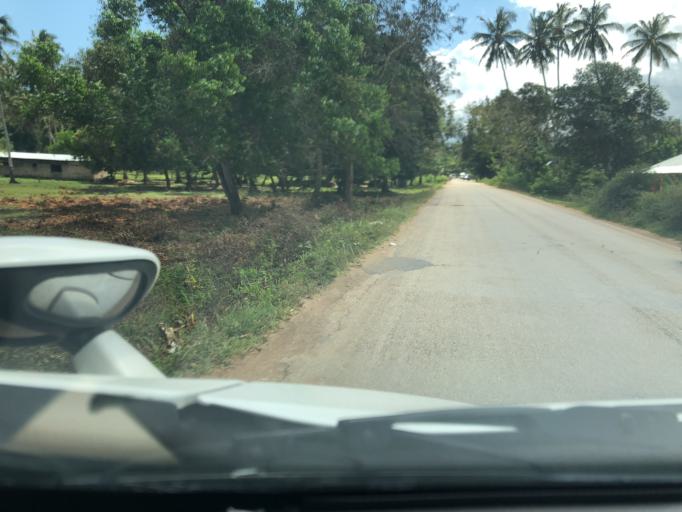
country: TZ
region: Zanzibar Central/South
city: Koani
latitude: -6.0657
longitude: 39.2516
